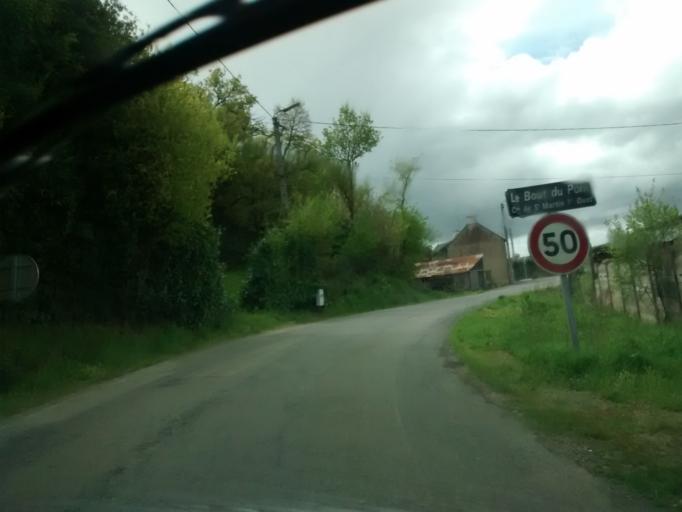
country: FR
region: Brittany
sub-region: Departement du Morbihan
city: Ruffiac
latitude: 47.7707
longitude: -2.3139
